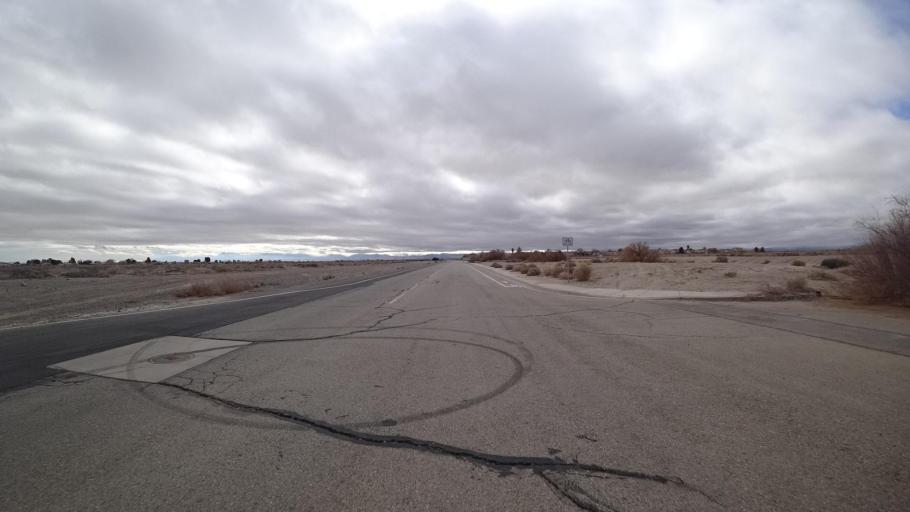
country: US
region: California
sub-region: Kern County
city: Rosamond
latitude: 34.8533
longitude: -118.1760
